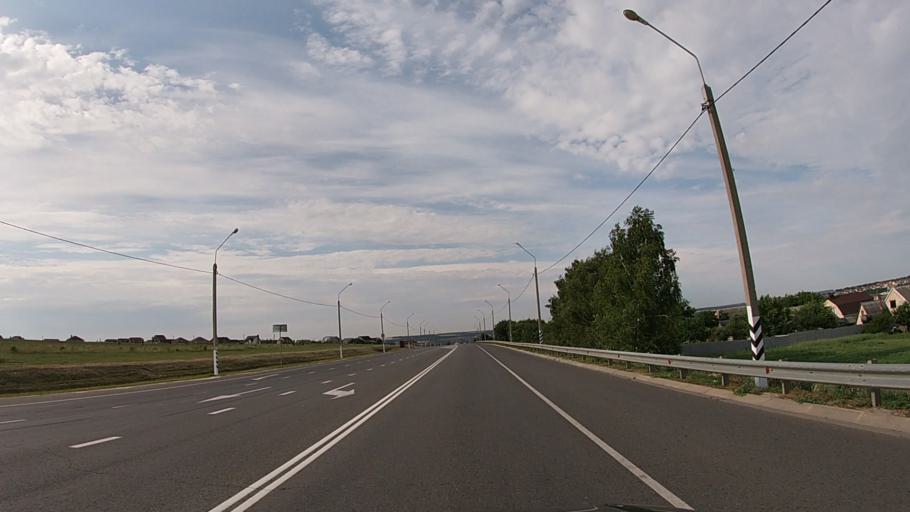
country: RU
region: Belgorod
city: Severnyy
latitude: 50.6520
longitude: 36.4673
